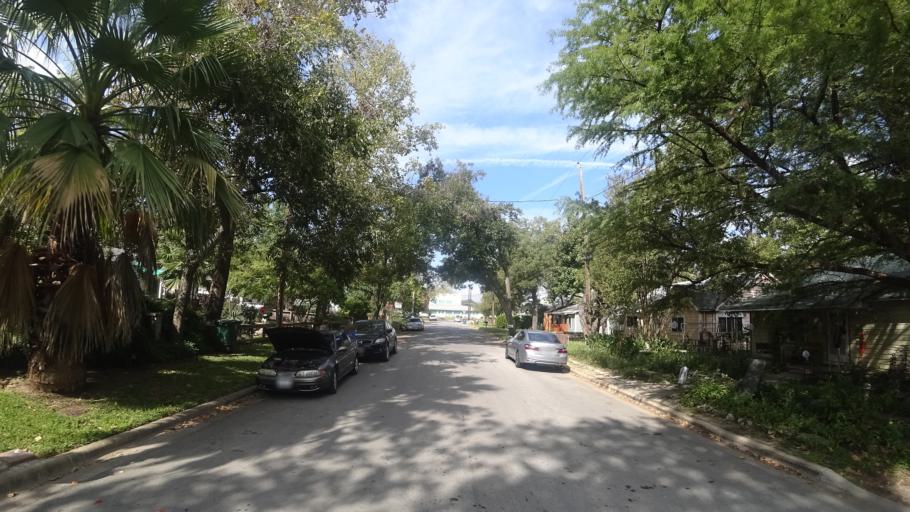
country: US
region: Texas
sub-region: Travis County
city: Austin
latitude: 30.2588
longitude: -97.6984
